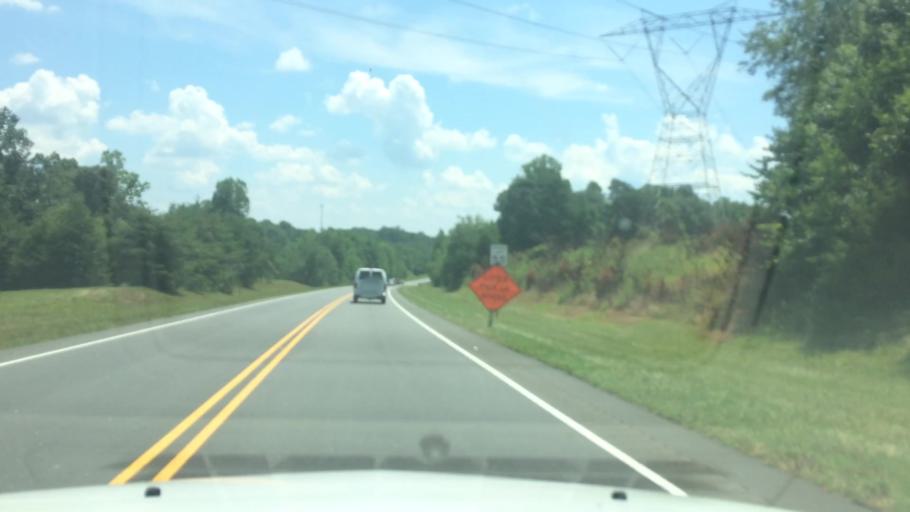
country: US
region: North Carolina
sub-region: Alexander County
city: Stony Point
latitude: 35.8339
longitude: -81.0179
